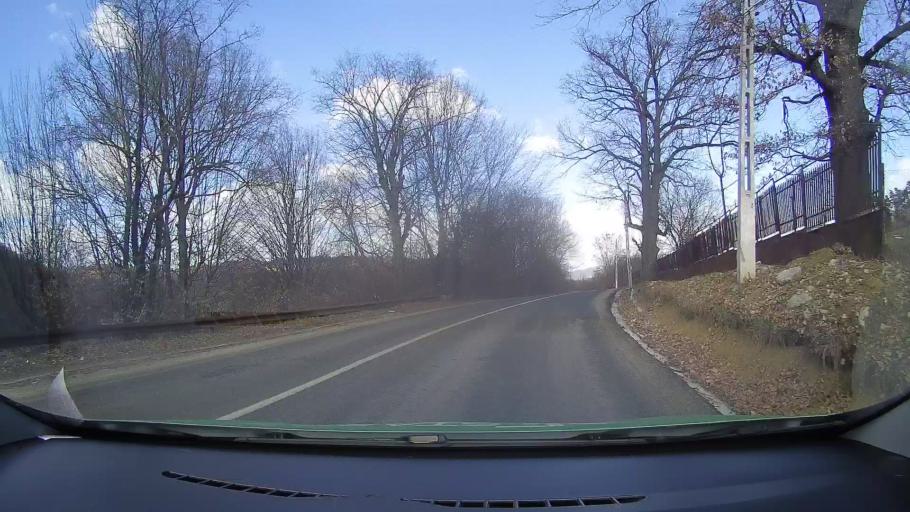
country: RO
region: Dambovita
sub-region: Comuna Runcu
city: Badeni
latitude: 45.1382
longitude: 25.4028
